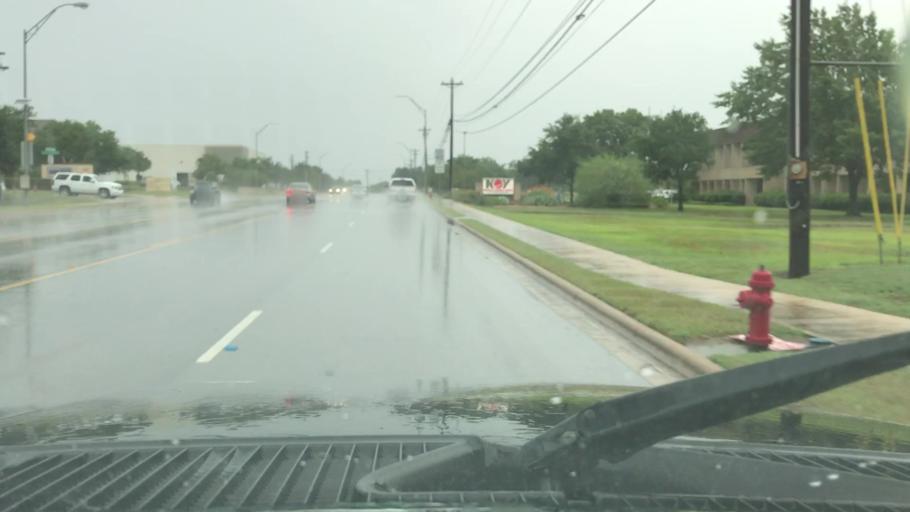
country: US
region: Texas
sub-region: Williamson County
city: Cedar Park
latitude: 30.4896
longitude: -97.8290
